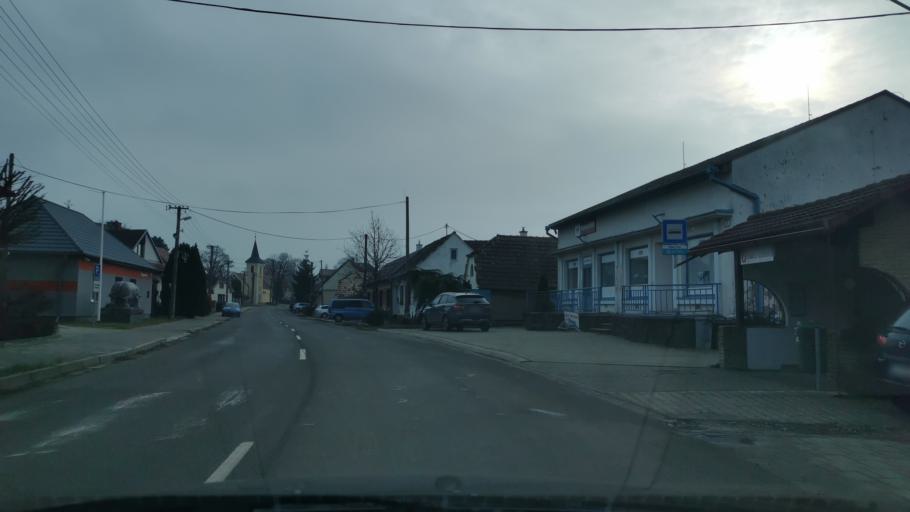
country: SK
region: Trnavsky
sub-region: Okres Senica
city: Senica
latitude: 48.7072
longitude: 17.3385
